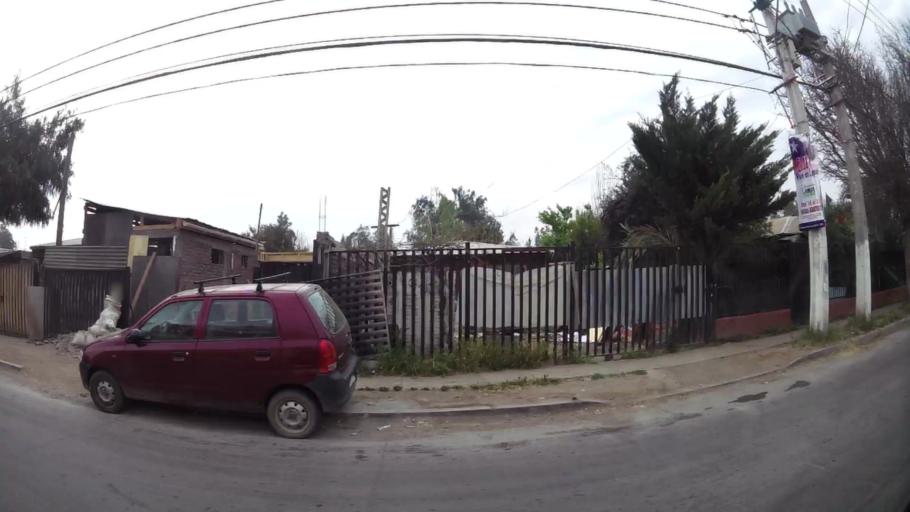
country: CL
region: Santiago Metropolitan
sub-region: Provincia de Chacabuco
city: Lampa
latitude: -33.2349
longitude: -70.8068
